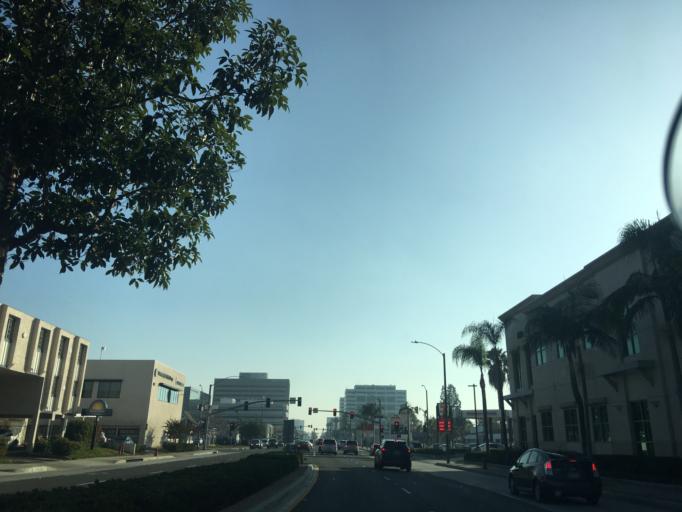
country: US
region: California
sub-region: Orange County
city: Orange
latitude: 33.7847
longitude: -117.8674
